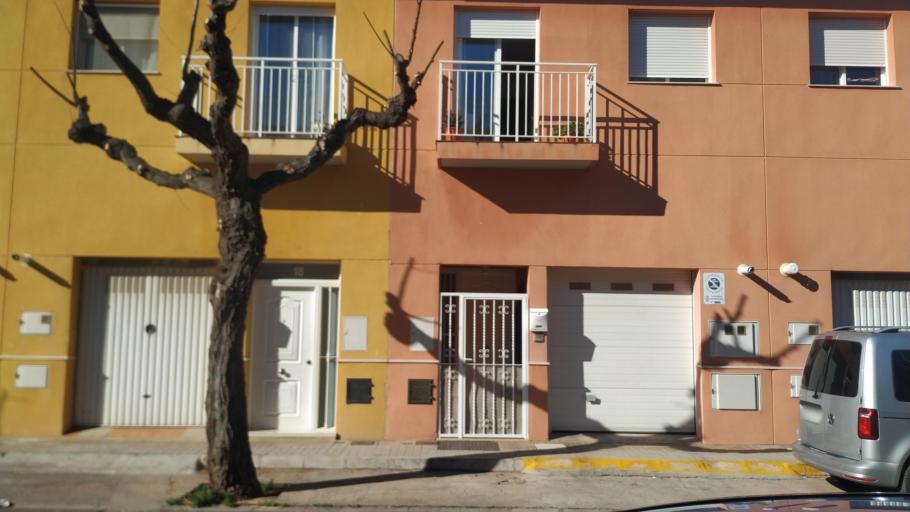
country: ES
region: Valencia
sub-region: Provincia de Valencia
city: Massamagrell
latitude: 39.5683
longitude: -0.3297
